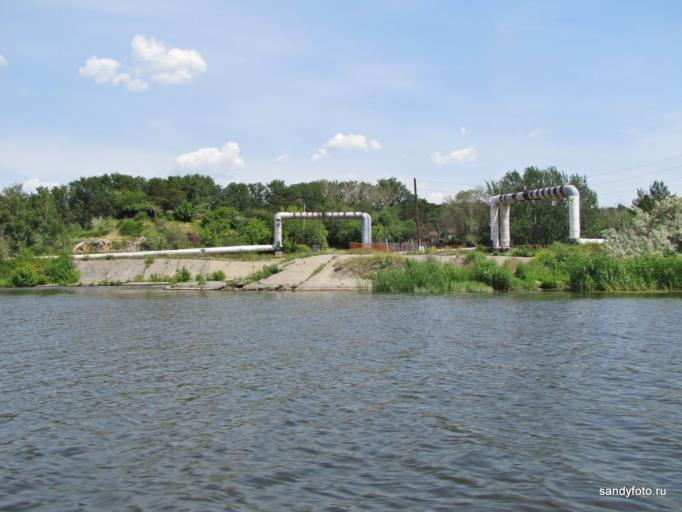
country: RU
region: Chelyabinsk
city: Troitsk
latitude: 54.0496
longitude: 61.6150
